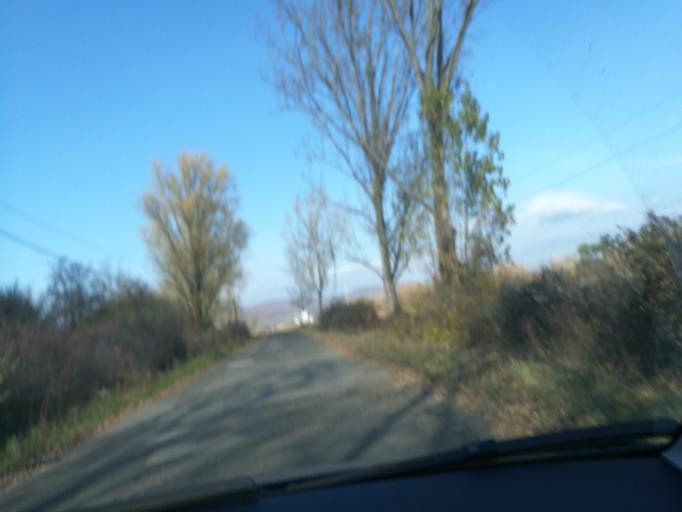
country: HU
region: Nograd
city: Paszto
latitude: 47.8998
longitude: 19.6904
